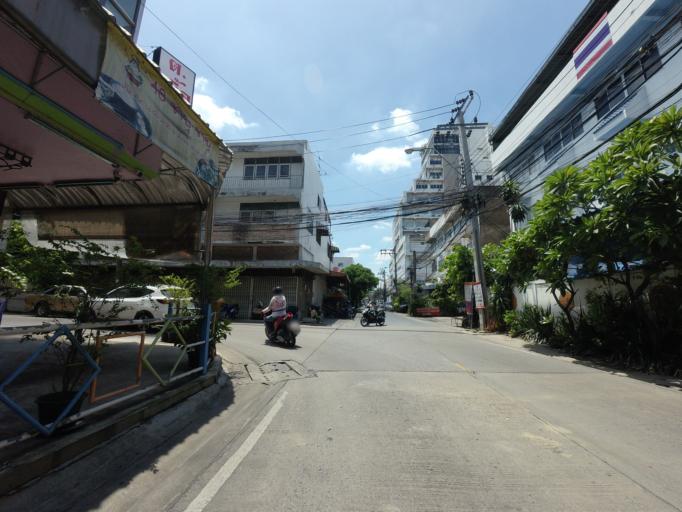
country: TH
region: Bangkok
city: Huai Khwang
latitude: 13.7938
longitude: 100.5850
